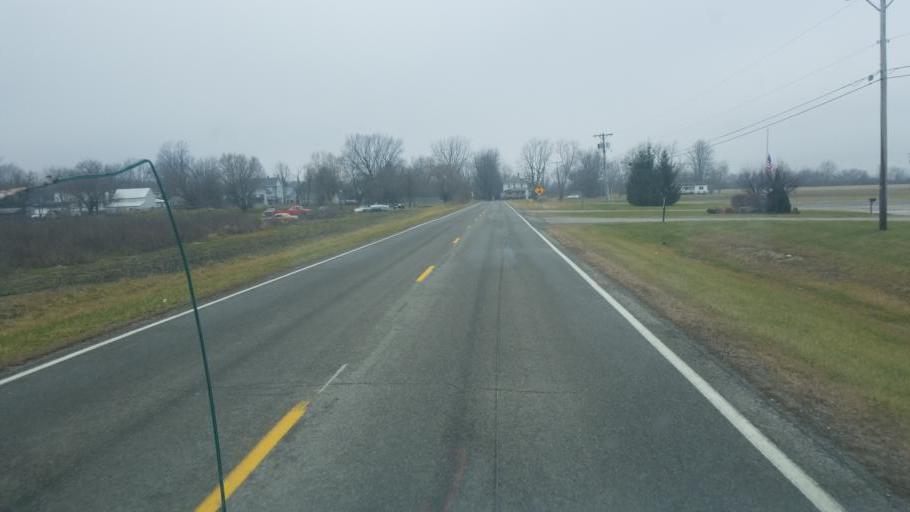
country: US
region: Ohio
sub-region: Champaign County
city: North Lewisburg
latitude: 40.3316
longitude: -83.5754
